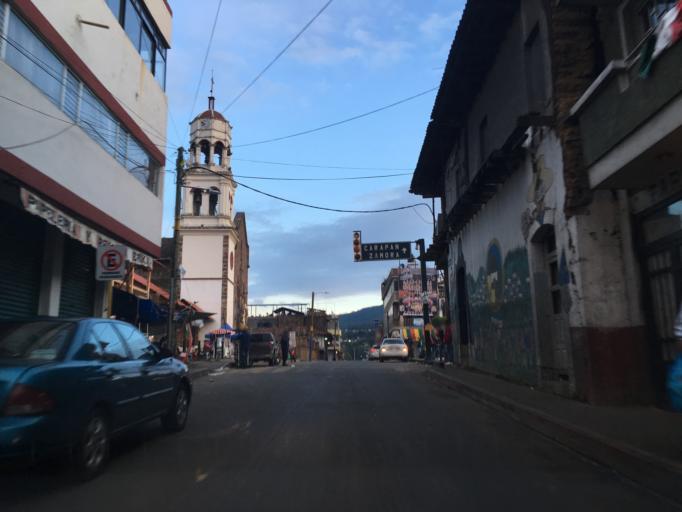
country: MX
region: Michoacan
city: Cheran
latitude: 19.6876
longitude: -101.9550
